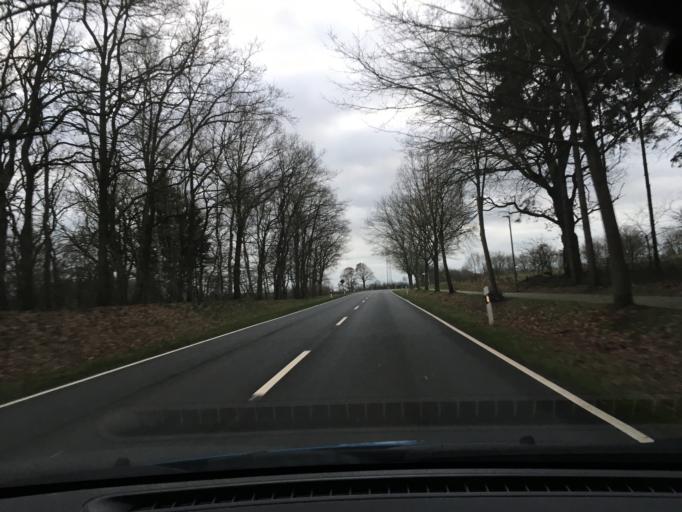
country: DE
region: Schleswig-Holstein
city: Mehlbek
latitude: 53.9941
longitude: 9.4398
